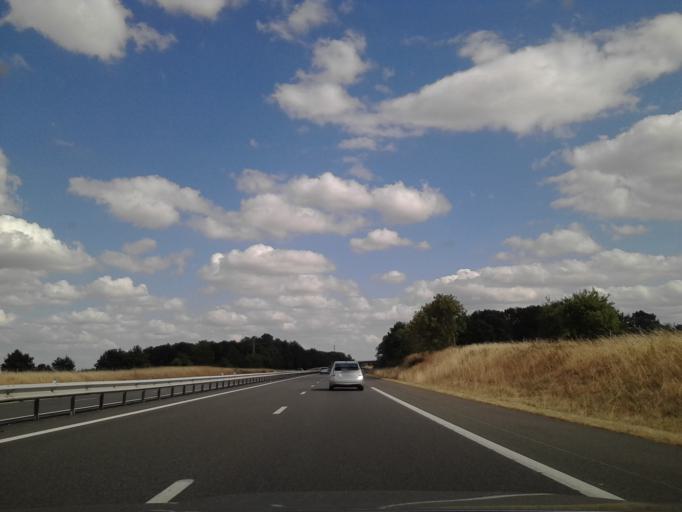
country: FR
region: Auvergne
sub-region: Departement de l'Allier
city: Vallon-en-Sully
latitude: 46.5250
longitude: 2.5691
